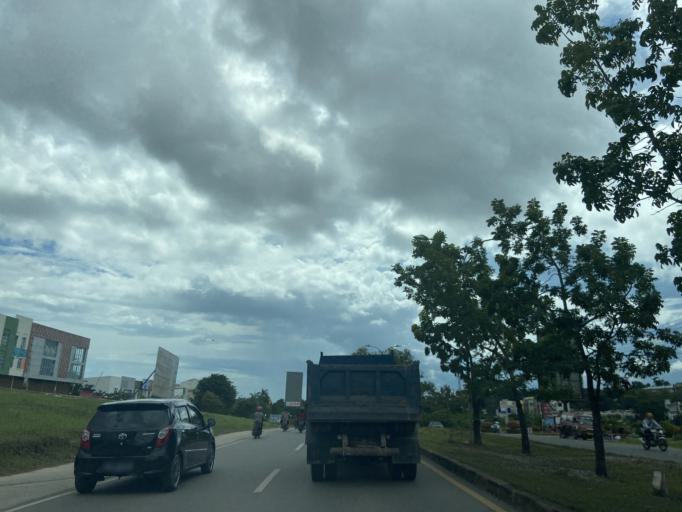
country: SG
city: Singapore
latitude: 1.0402
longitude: 103.9939
